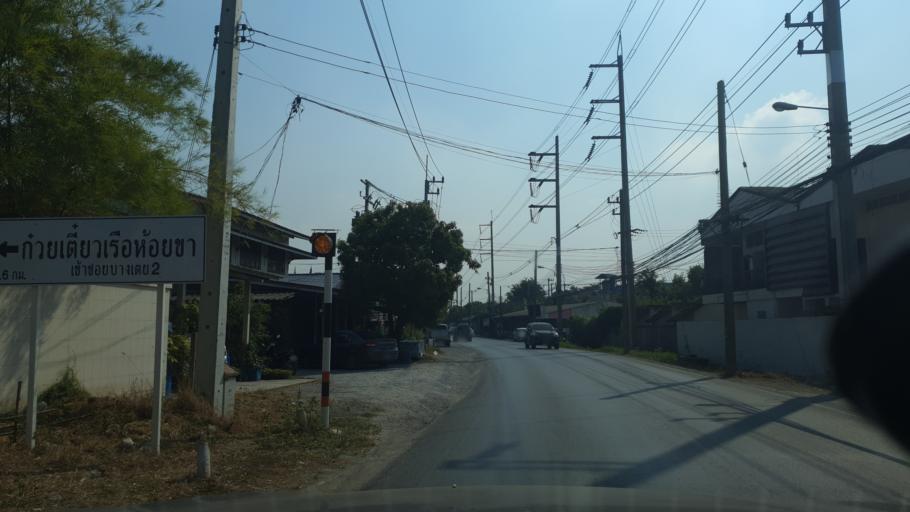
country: TH
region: Nakhon Pathom
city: Salaya
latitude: 13.7749
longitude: 100.2785
